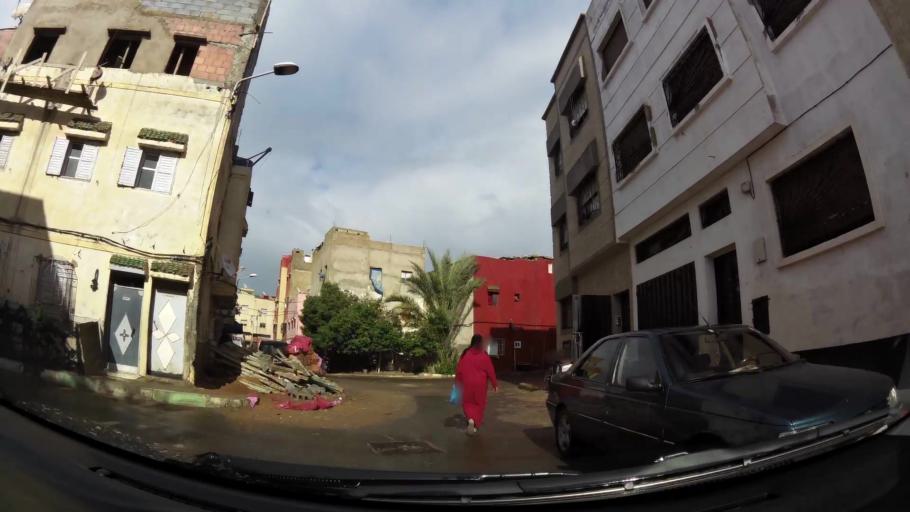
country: MA
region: Grand Casablanca
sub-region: Casablanca
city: Casablanca
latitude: 33.5632
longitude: -7.6946
